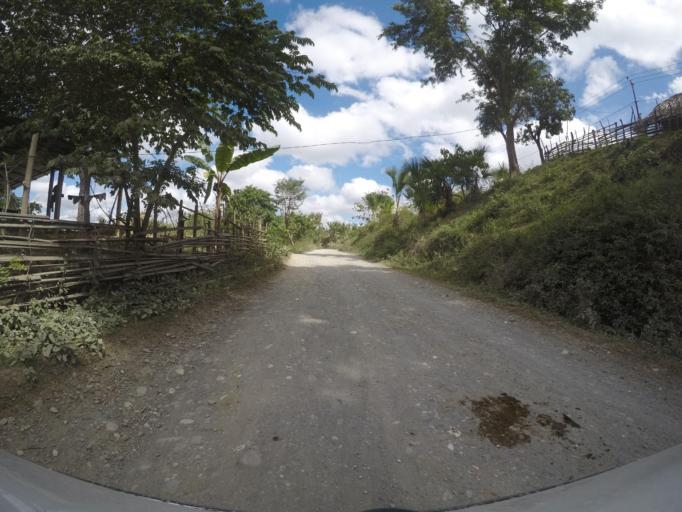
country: TL
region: Viqueque
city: Viqueque
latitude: -8.8666
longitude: 126.3367
